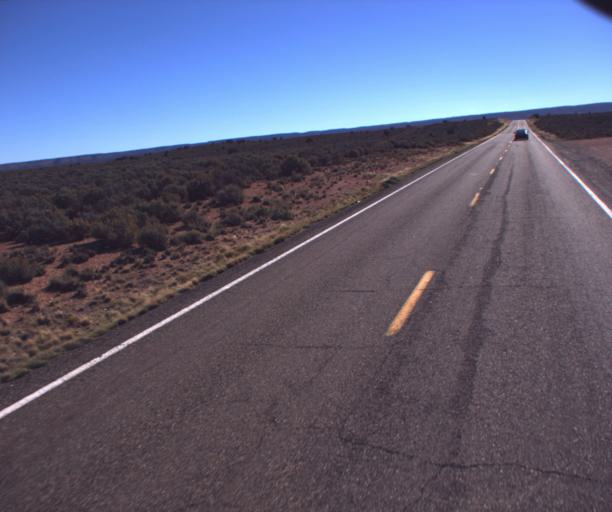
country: US
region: Arizona
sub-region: Coconino County
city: Fredonia
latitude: 36.8829
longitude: -112.3423
